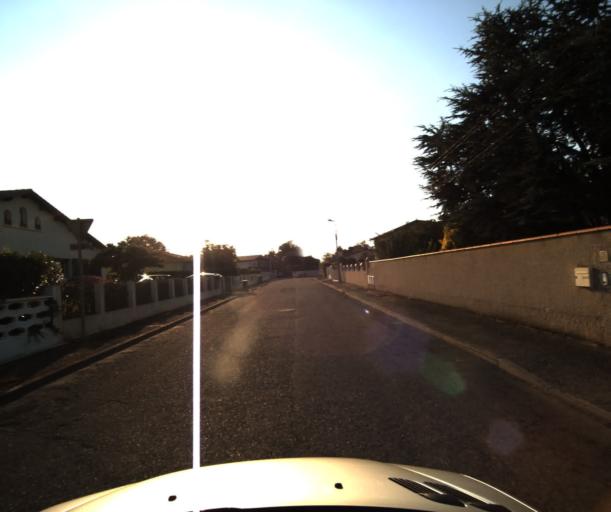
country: FR
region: Midi-Pyrenees
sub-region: Departement de la Haute-Garonne
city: Lacroix-Falgarde
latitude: 43.4869
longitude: 1.3905
